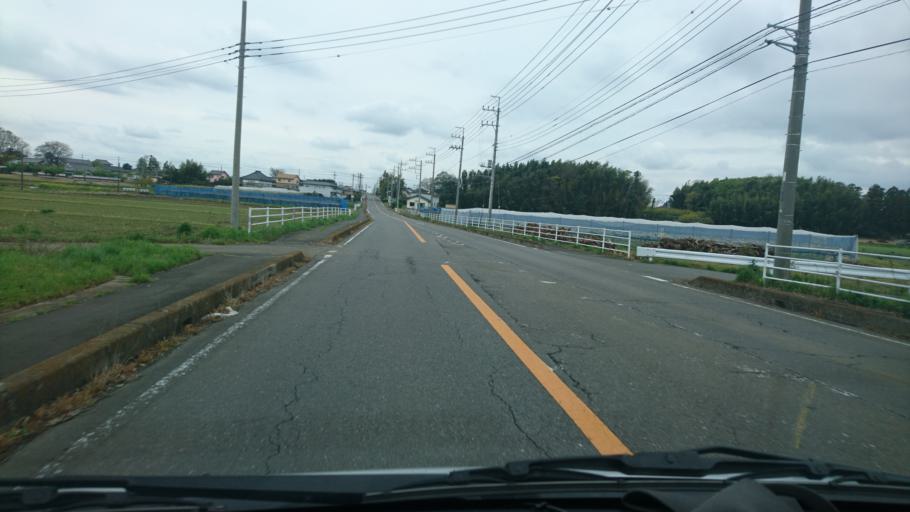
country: JP
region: Ibaraki
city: Yuki
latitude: 36.2608
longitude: 139.9276
